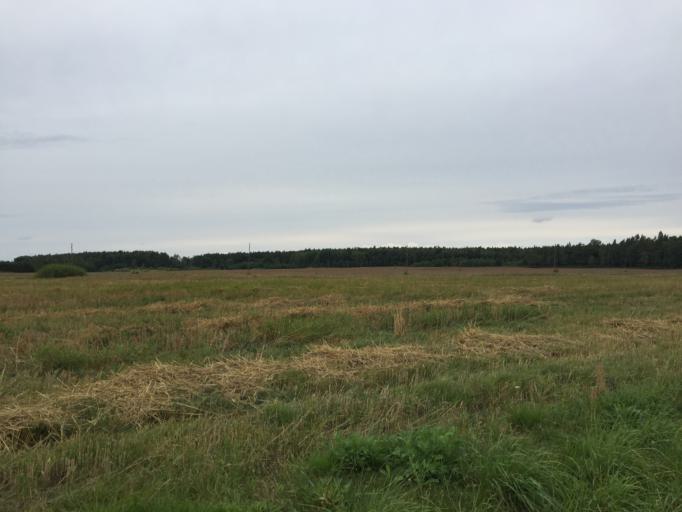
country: LV
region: Jaunpils
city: Jaunpils
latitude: 56.7293
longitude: 23.1461
